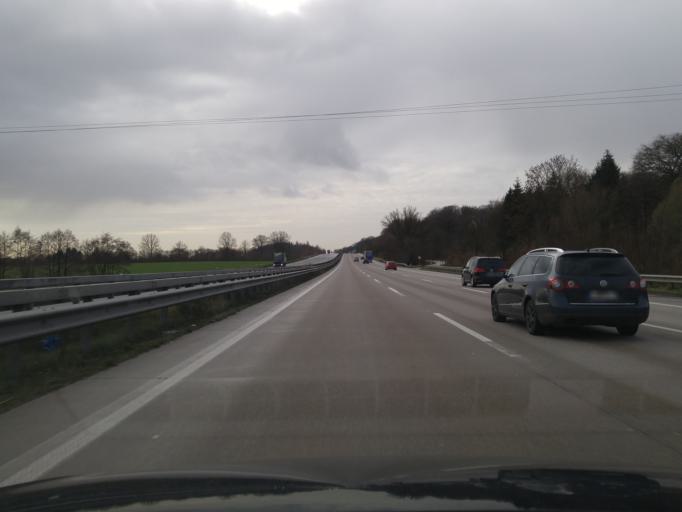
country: DE
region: Schleswig-Holstein
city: Lasbek
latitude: 53.7557
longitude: 10.3739
